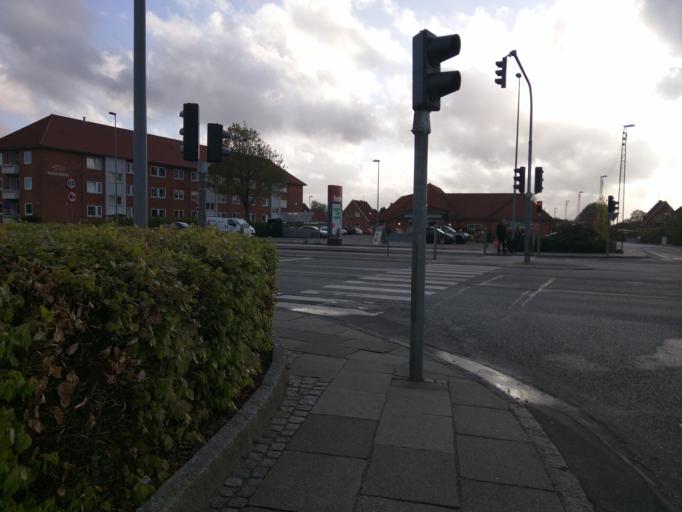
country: DK
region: Central Jutland
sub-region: Viborg Kommune
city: Viborg
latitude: 56.4543
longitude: 9.3933
